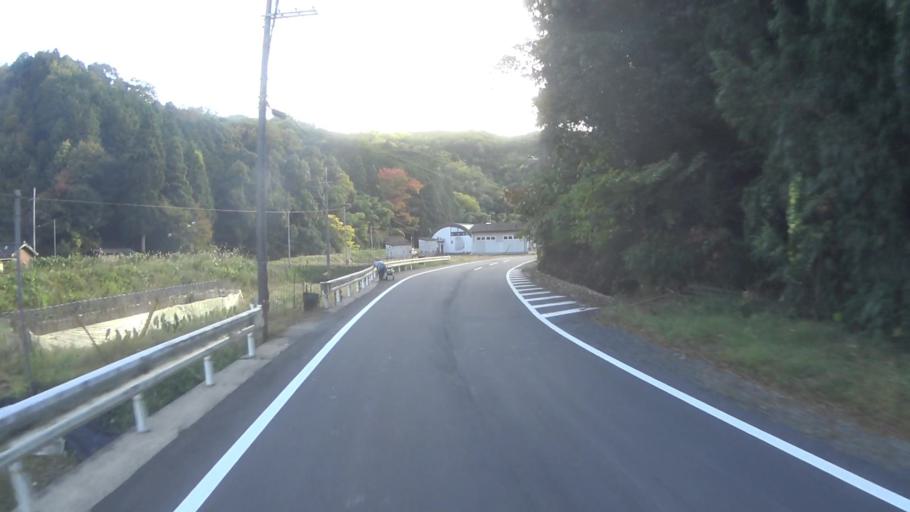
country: JP
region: Kyoto
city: Miyazu
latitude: 35.4576
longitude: 135.2299
